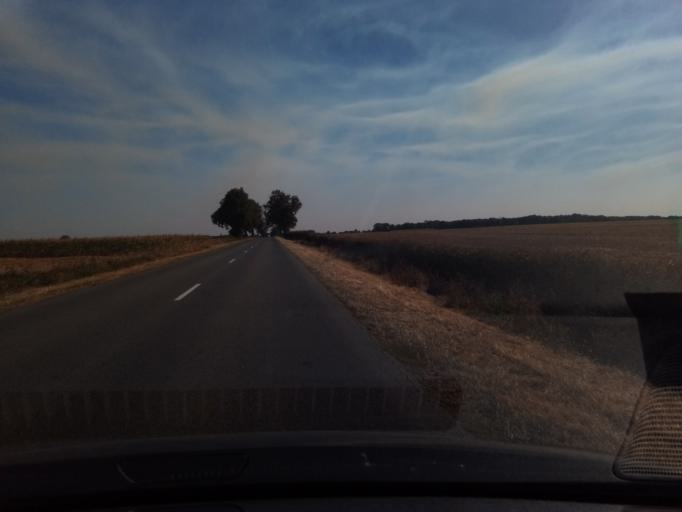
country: FR
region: Poitou-Charentes
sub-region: Departement de la Vienne
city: Saint-Savin
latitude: 46.4997
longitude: 0.7794
